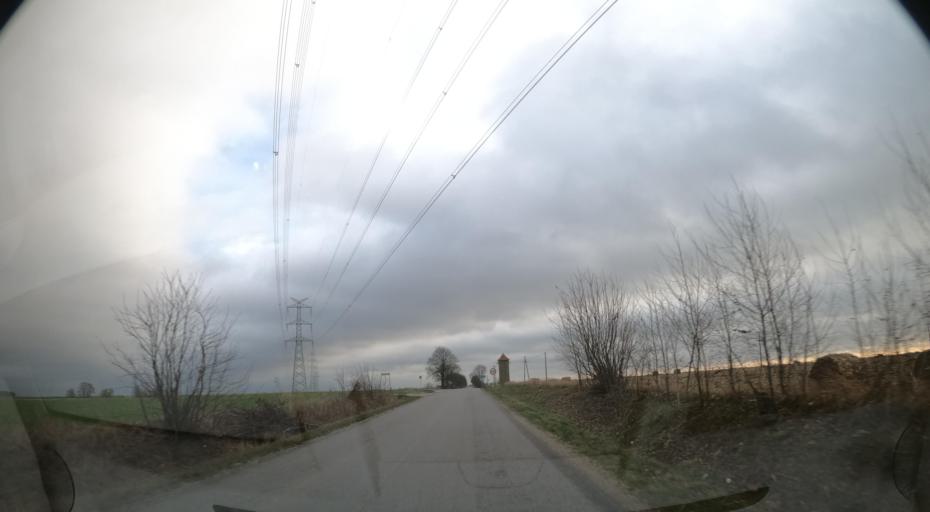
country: PL
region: Kujawsko-Pomorskie
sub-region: Powiat nakielski
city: Sadki
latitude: 53.1780
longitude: 17.4144
